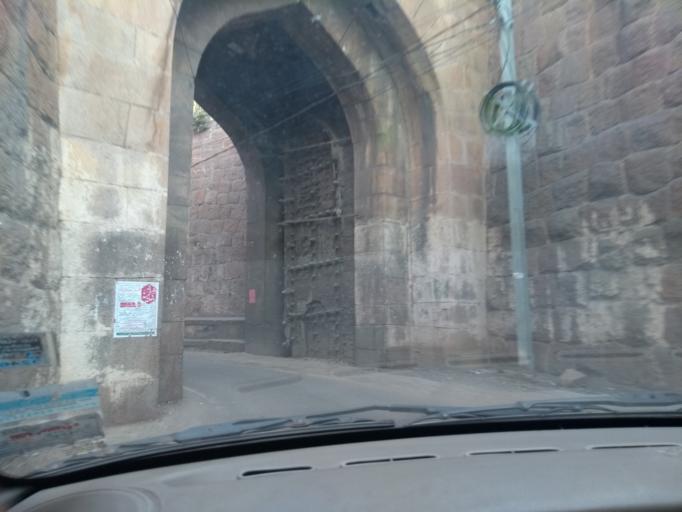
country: IN
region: Telangana
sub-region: Hyderabad
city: Hyderabad
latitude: 17.3792
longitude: 78.4128
